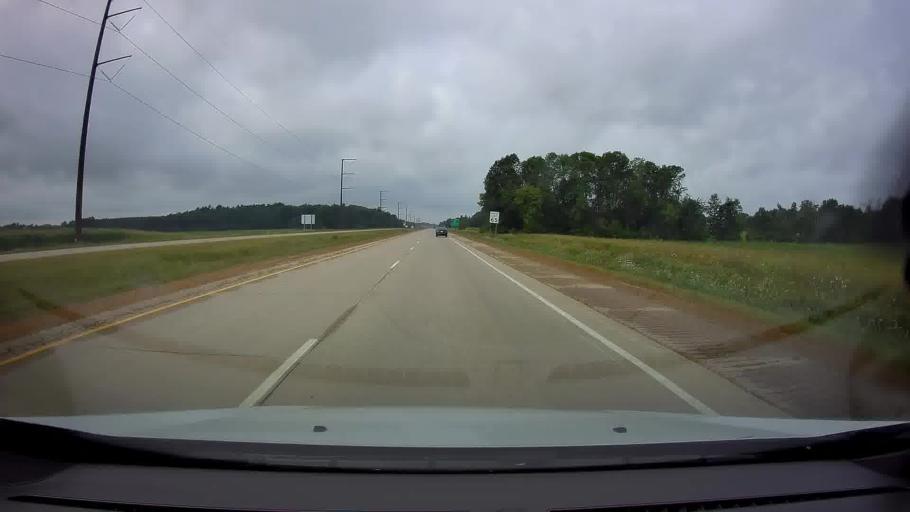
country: US
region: Wisconsin
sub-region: Shawano County
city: Shawano
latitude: 44.7549
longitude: -88.5809
